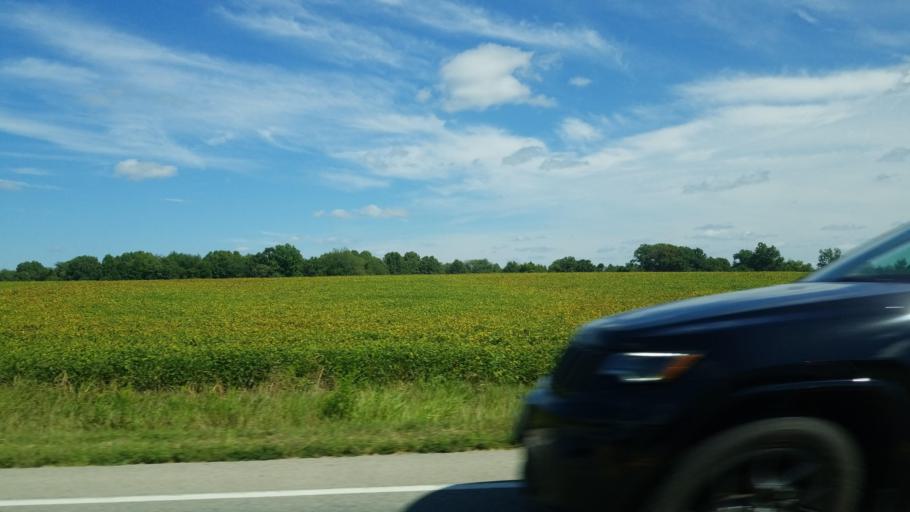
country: US
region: Illinois
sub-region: Williamson County
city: Marion
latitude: 37.7682
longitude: -88.9329
